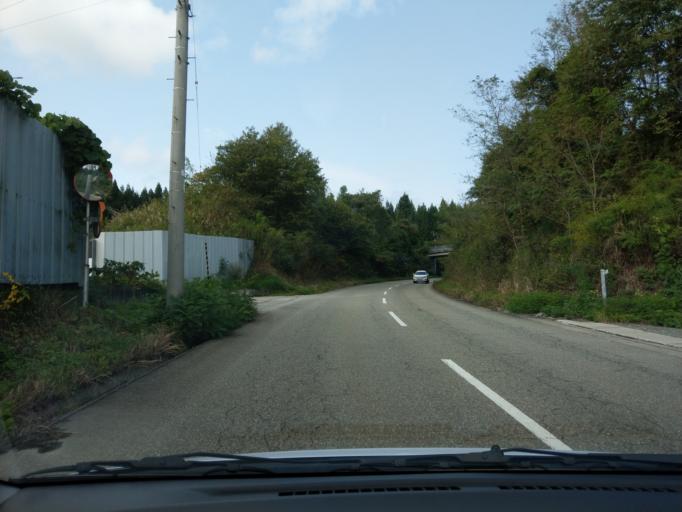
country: JP
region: Akita
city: Omagari
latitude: 39.5202
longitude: 140.2976
